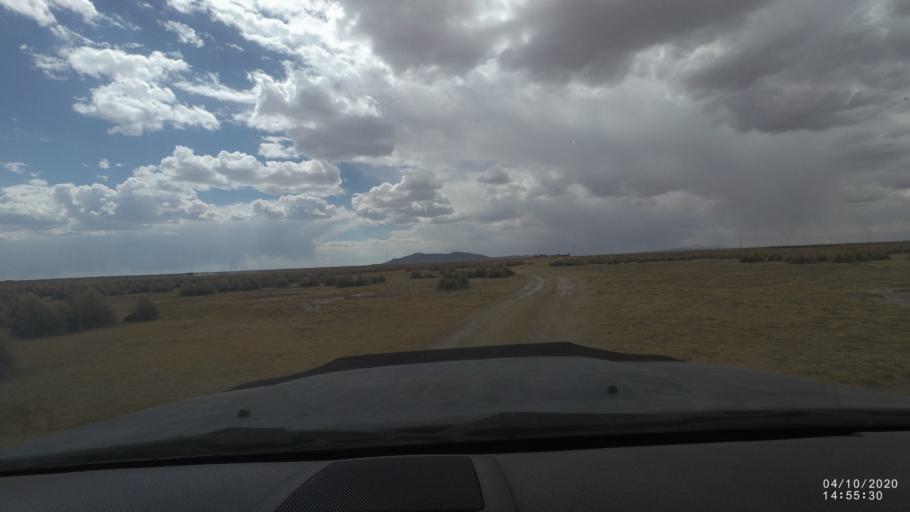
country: BO
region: Oruro
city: Poopo
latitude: -18.6840
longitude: -67.5130
